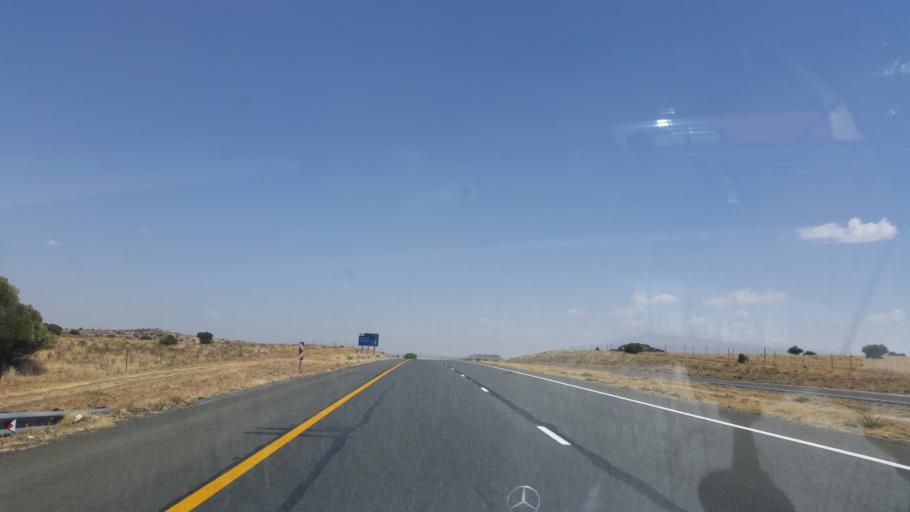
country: ZA
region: Orange Free State
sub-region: Lejweleputswa District Municipality
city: Brandfort
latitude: -28.9243
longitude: 26.4357
